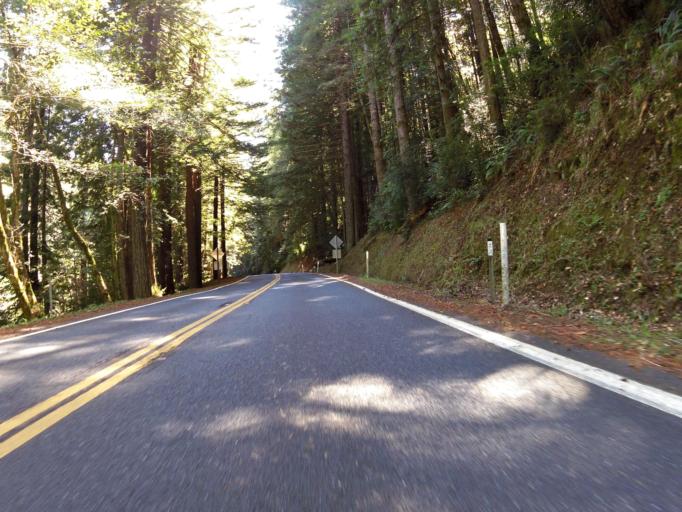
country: US
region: California
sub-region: Humboldt County
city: Redway
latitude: 39.7981
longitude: -123.8204
